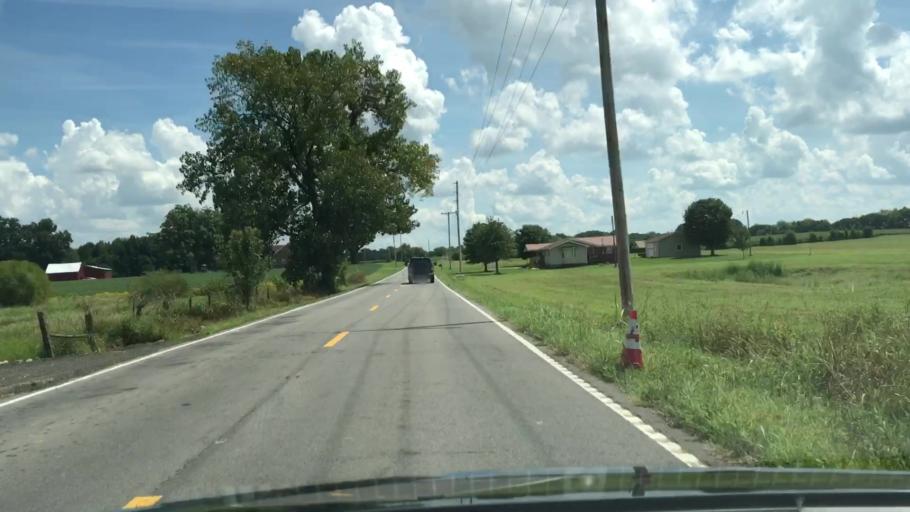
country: US
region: Tennessee
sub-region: Robertson County
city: Springfield
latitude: 36.5585
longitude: -86.8336
